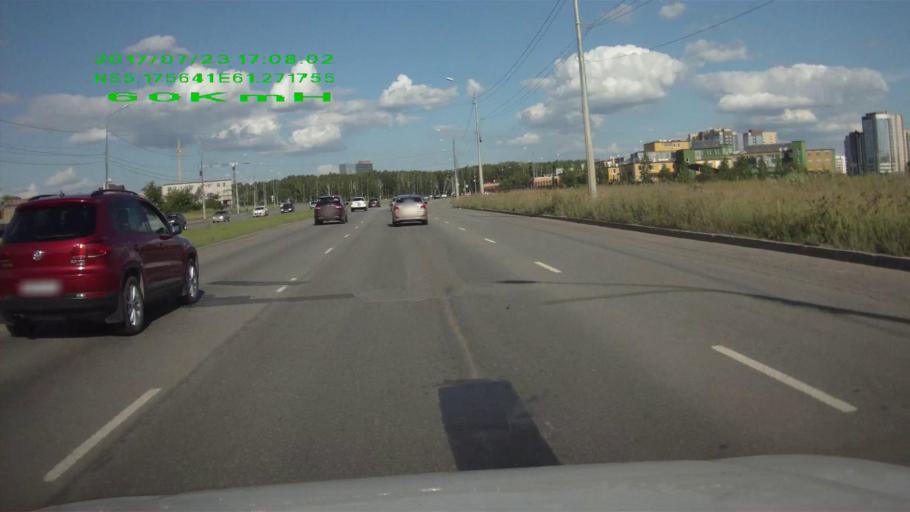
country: RU
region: Chelyabinsk
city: Roshchino
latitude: 55.1758
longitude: 61.2730
